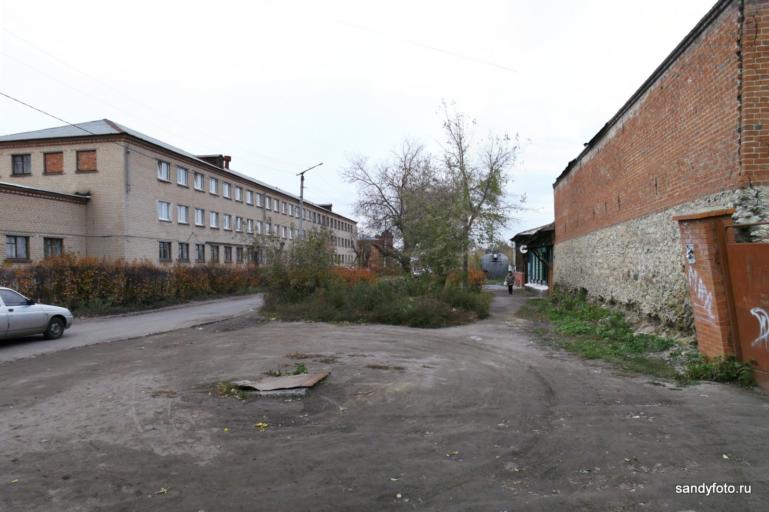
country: RU
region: Chelyabinsk
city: Troitsk
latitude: 54.0863
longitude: 61.5505
